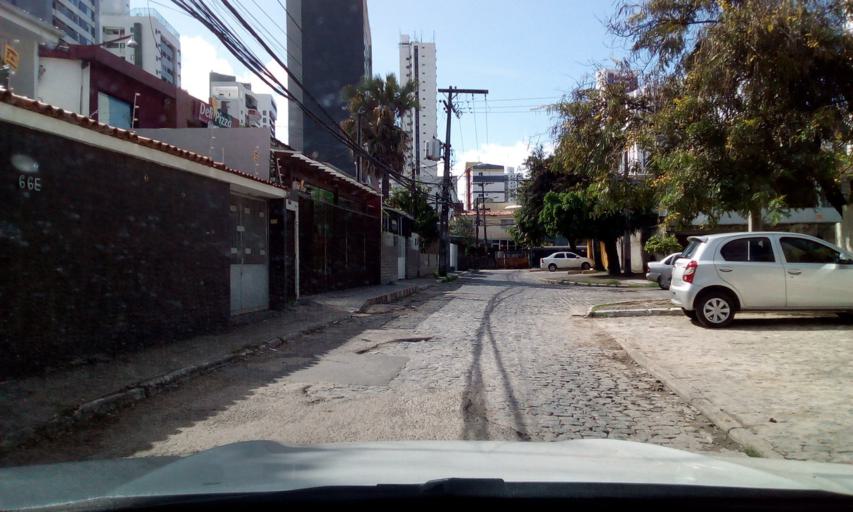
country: BR
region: Pernambuco
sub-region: Recife
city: Recife
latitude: -8.1282
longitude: -34.9056
